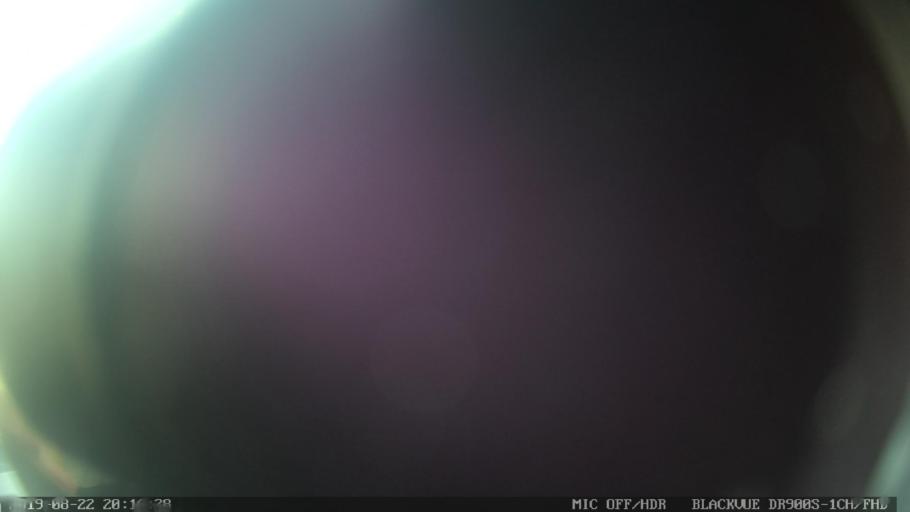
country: PT
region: Guarda
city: Alcains
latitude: 39.9244
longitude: -7.4534
